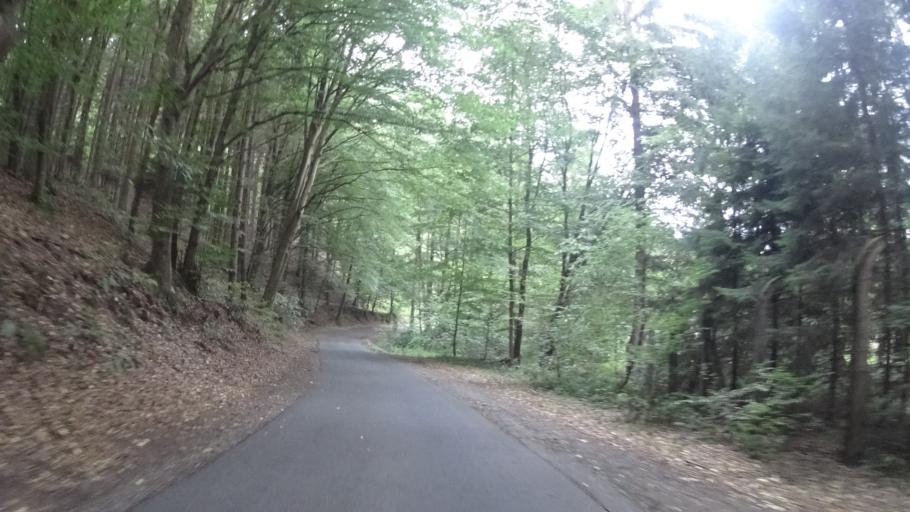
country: CZ
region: Olomoucky
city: Zabreh
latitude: 49.8683
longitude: 16.7898
